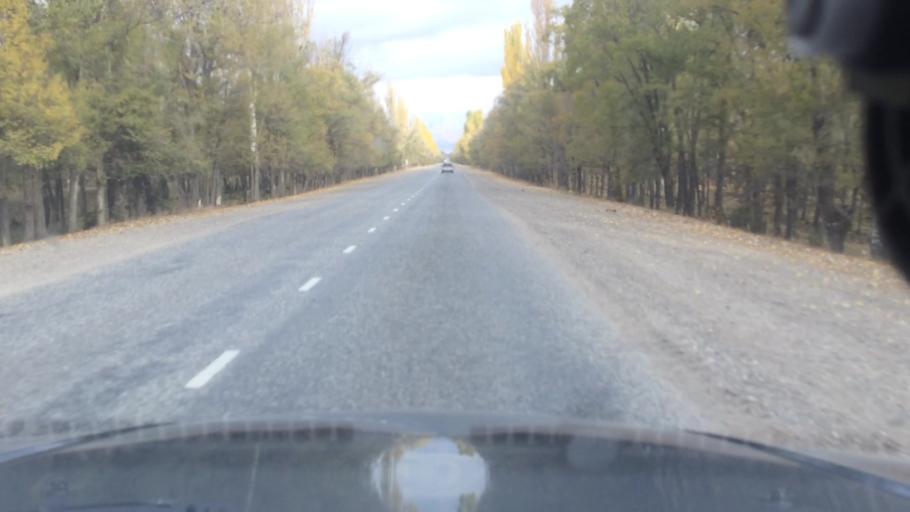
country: KG
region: Ysyk-Koel
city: Tyup
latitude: 42.6317
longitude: 78.3603
